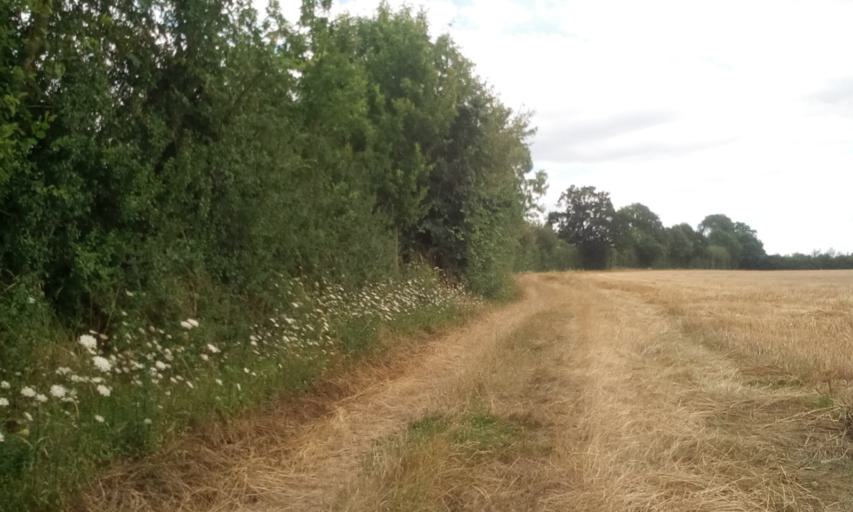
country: FR
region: Lower Normandy
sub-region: Departement du Calvados
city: Troarn
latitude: 49.1666
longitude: -0.1913
